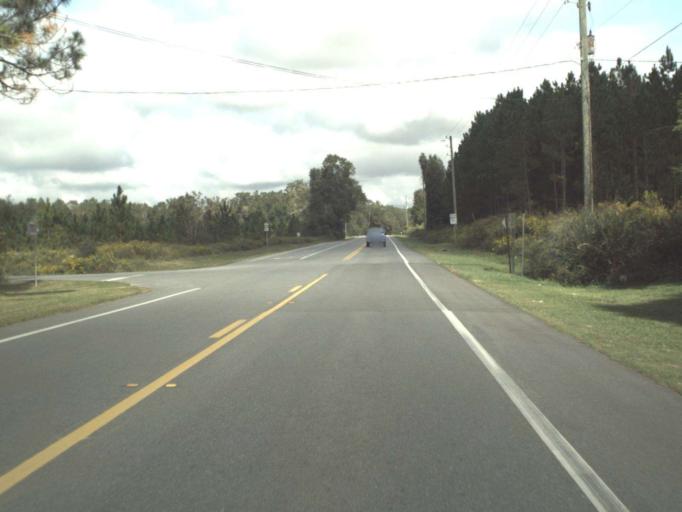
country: US
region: Florida
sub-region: Jackson County
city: Marianna
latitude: 30.6259
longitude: -85.1536
